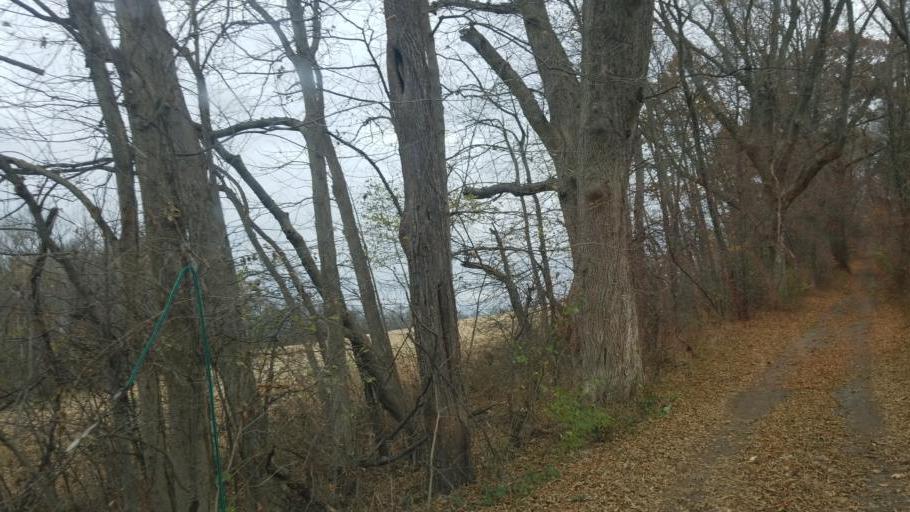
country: US
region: Ohio
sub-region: Knox County
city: Fredericktown
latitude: 40.4466
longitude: -82.5292
